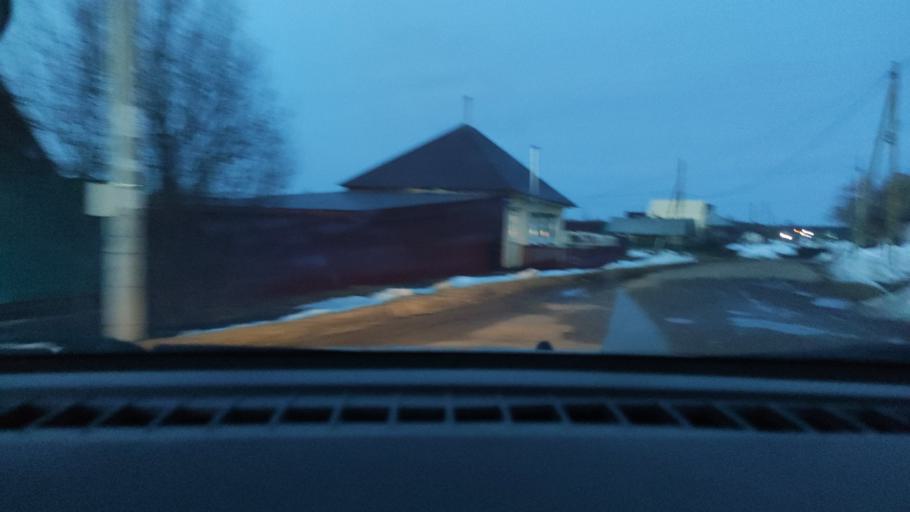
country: RU
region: Perm
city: Yug
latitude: 57.7283
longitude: 56.1652
